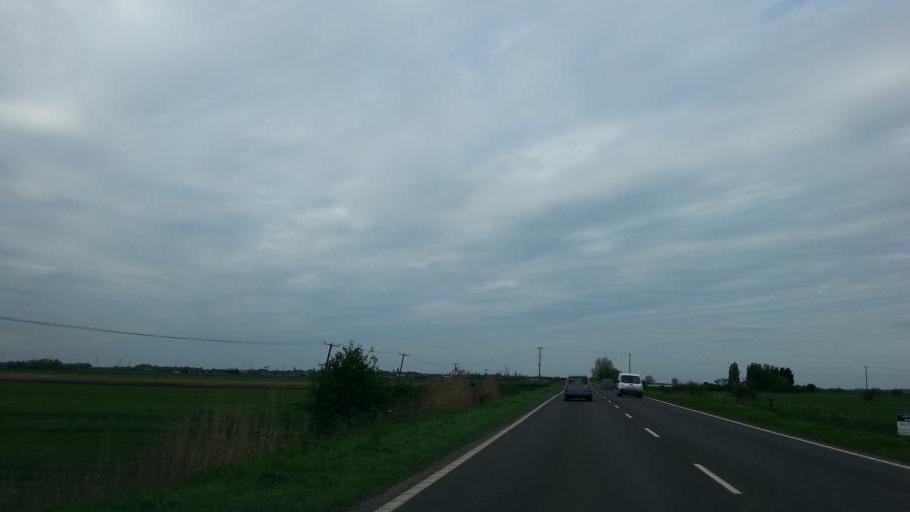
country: GB
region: England
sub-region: Cambridgeshire
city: Chatteris
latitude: 52.4692
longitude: 0.0469
